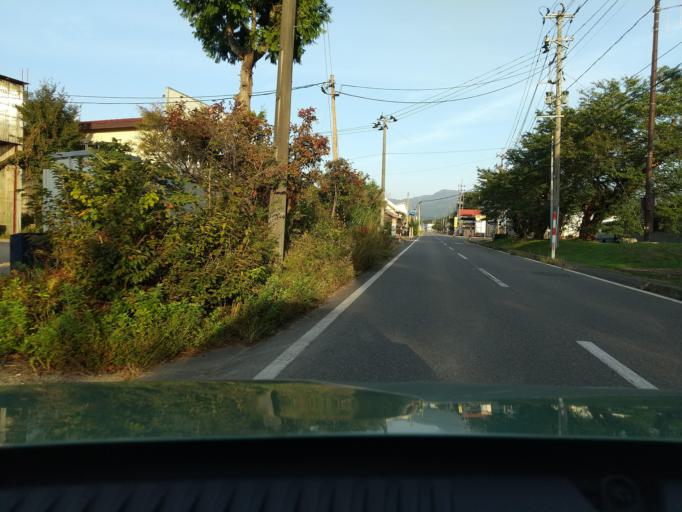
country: JP
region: Akita
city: Omagari
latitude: 39.4669
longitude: 140.5832
